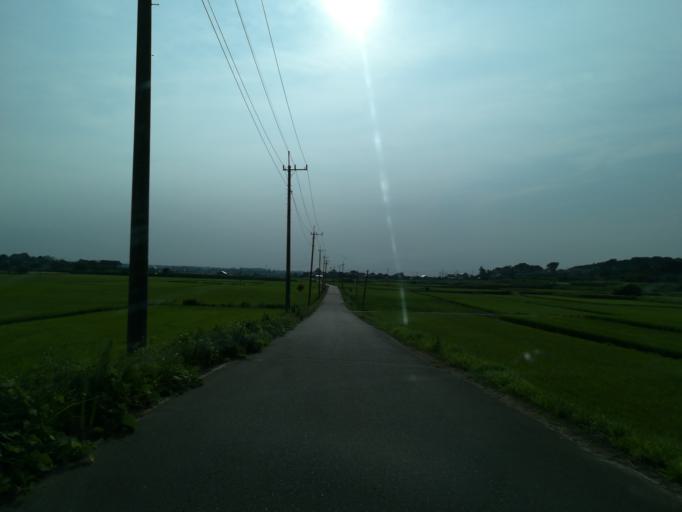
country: JP
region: Ibaraki
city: Tsukuba
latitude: 36.1982
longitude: 140.1033
